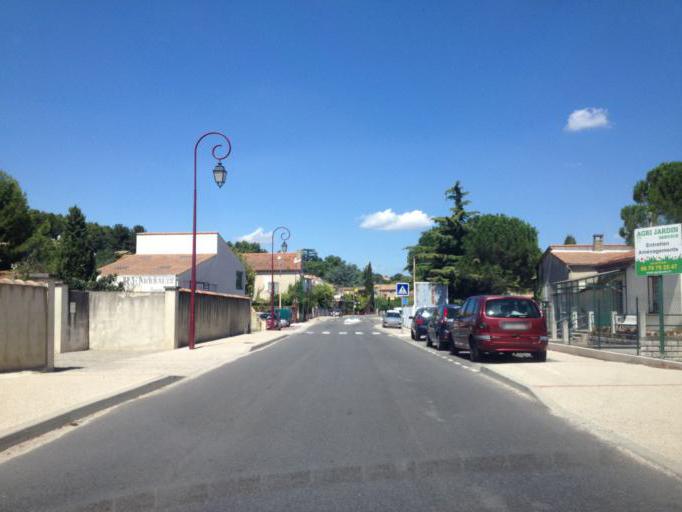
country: FR
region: Languedoc-Roussillon
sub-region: Departement du Gard
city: Sauveterre
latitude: 44.0211
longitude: 4.7935
